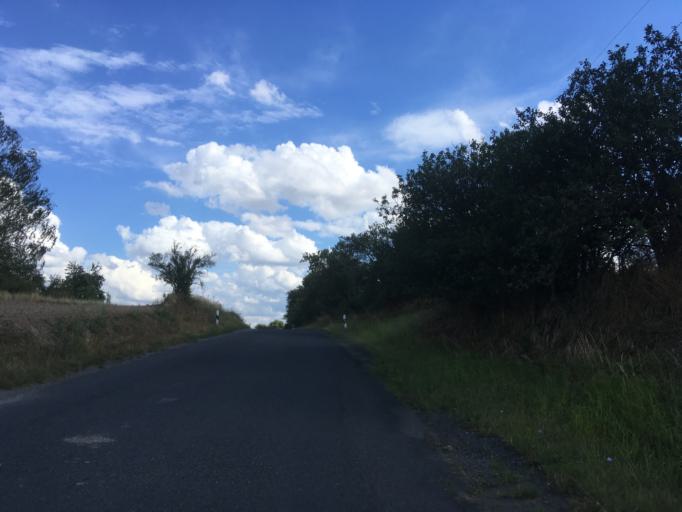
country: DE
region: Brandenburg
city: Angermunde
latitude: 52.9692
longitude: 13.9935
